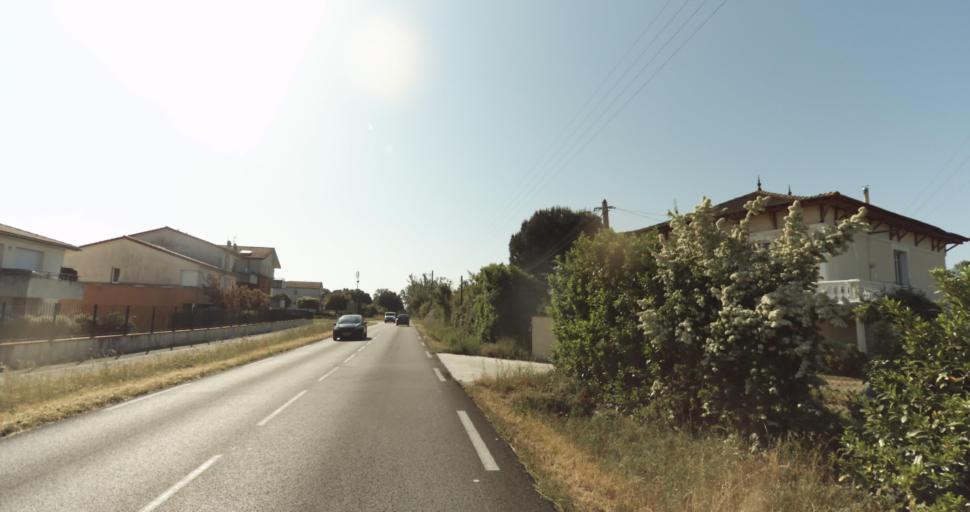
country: FR
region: Midi-Pyrenees
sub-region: Departement de la Haute-Garonne
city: Plaisance-du-Touch
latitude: 43.5528
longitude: 1.3113
